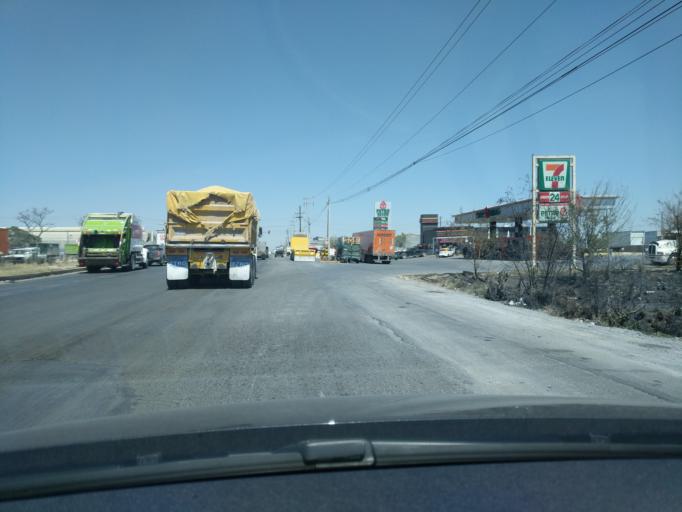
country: MX
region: Nuevo Leon
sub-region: Salinas Victoria
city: Simeprodeso (Colectivo Nuevo)
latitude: 25.8479
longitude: -100.2932
